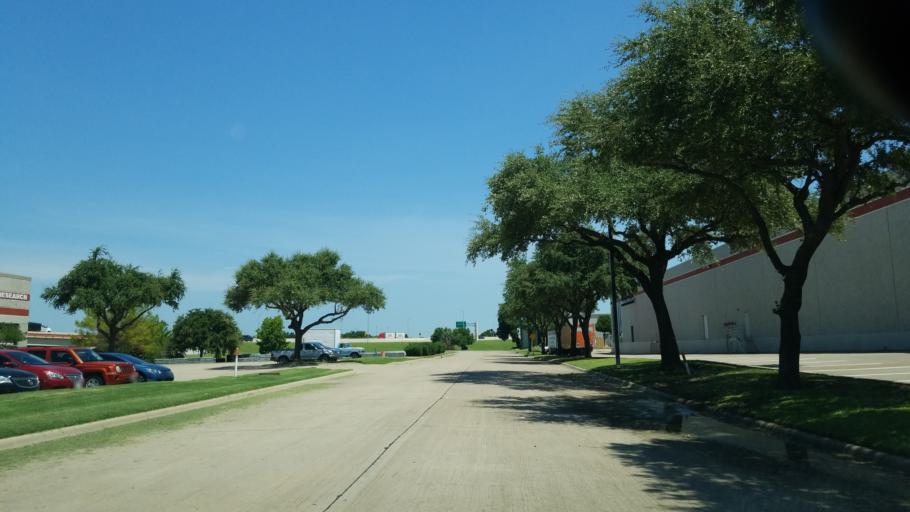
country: US
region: Texas
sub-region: Dallas County
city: Farmers Branch
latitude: 32.9417
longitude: -96.9280
